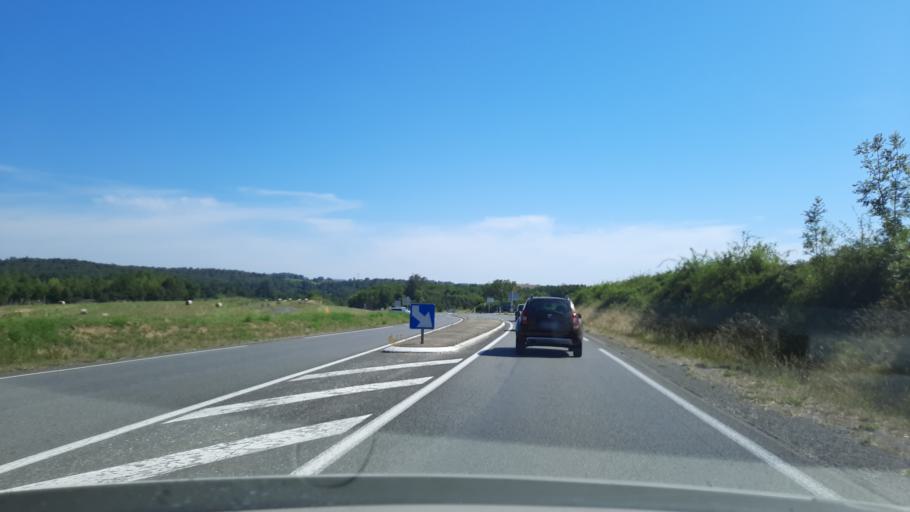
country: FR
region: Midi-Pyrenees
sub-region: Departement de l'Aveyron
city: Villefranche-de-Rouergue
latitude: 44.3351
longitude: 1.9358
